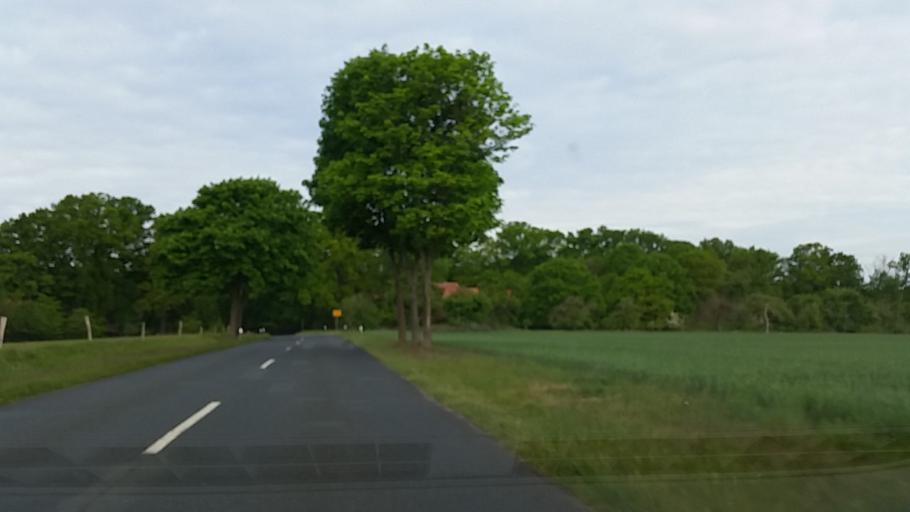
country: DE
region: Lower Saxony
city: Bodenteich
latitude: 52.8507
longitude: 10.6760
